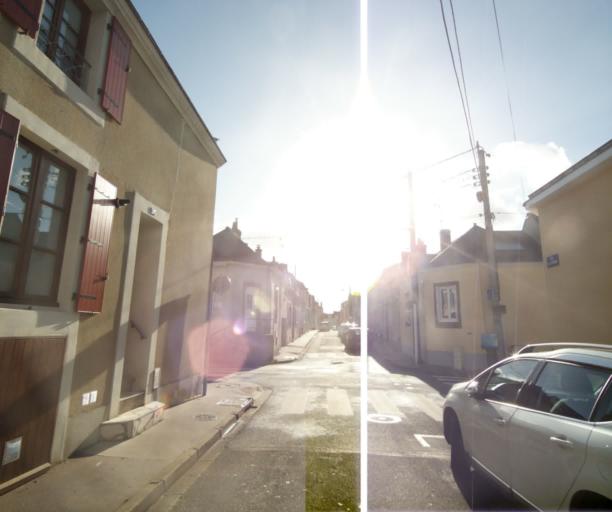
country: FR
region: Pays de la Loire
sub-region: Departement de la Sarthe
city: Le Mans
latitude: 48.0091
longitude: 0.1875
